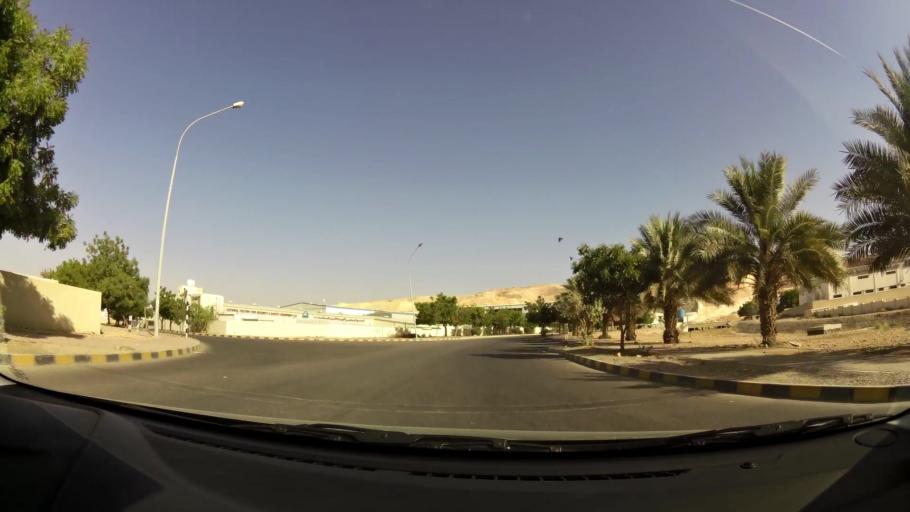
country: OM
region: Muhafazat Masqat
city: As Sib al Jadidah
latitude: 23.5536
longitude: 58.2227
